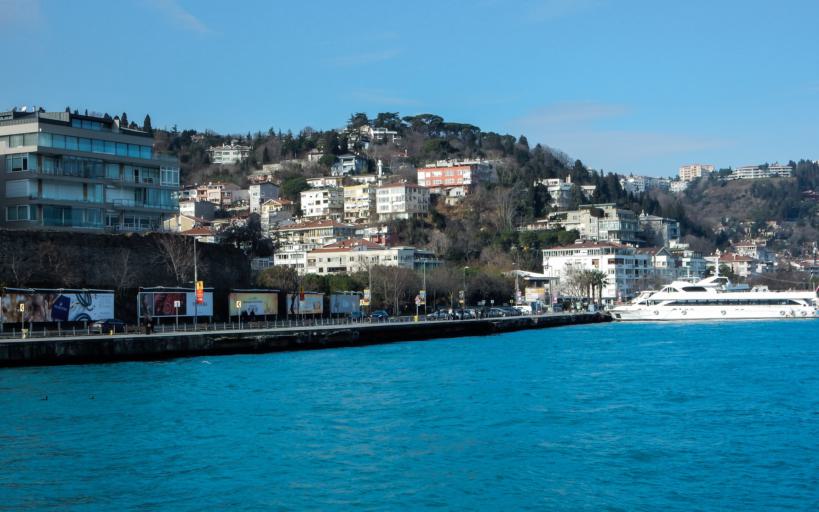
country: TR
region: Istanbul
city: UEskuedar
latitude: 41.0685
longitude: 29.0476
